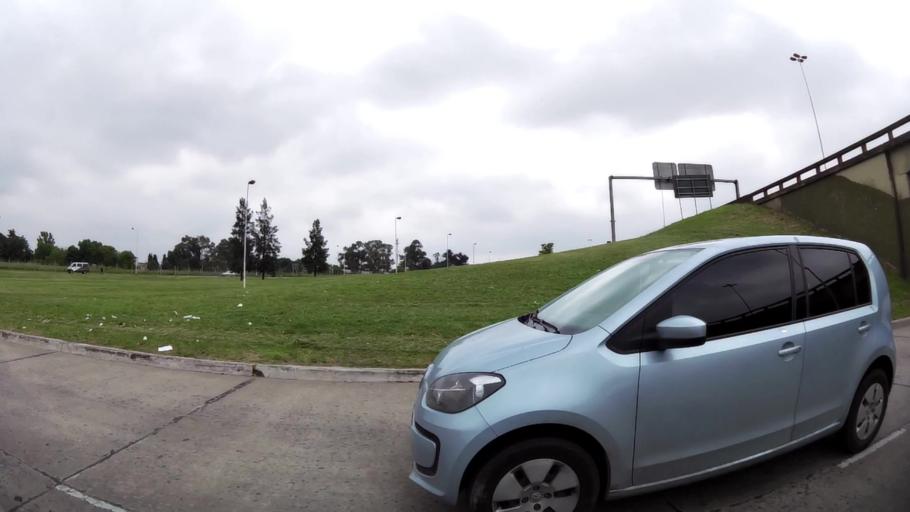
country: AR
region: Buenos Aires F.D.
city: Villa Lugano
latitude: -34.7269
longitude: -58.5151
